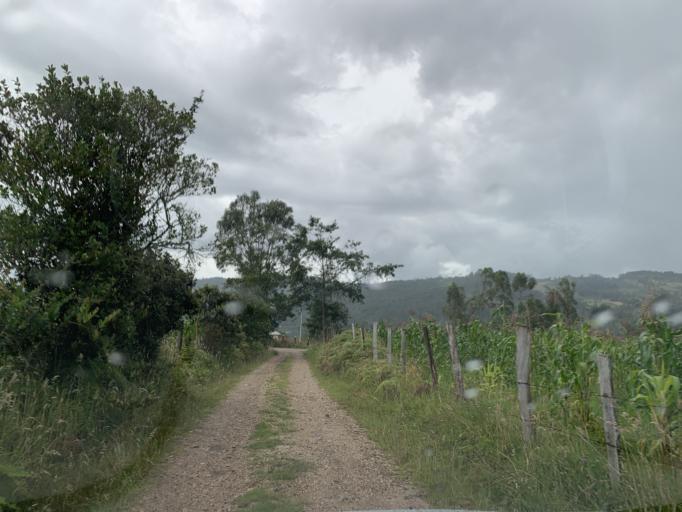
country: CO
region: Boyaca
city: Arcabuco
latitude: 5.7525
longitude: -73.4739
